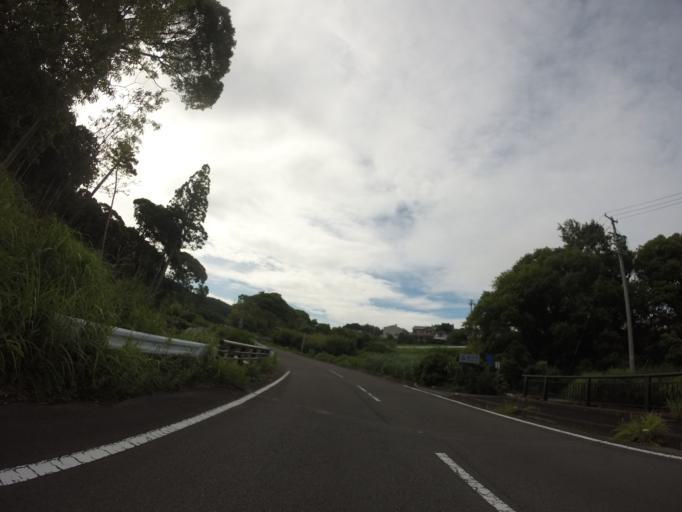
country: JP
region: Shizuoka
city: Kanaya
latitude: 34.7936
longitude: 138.1445
